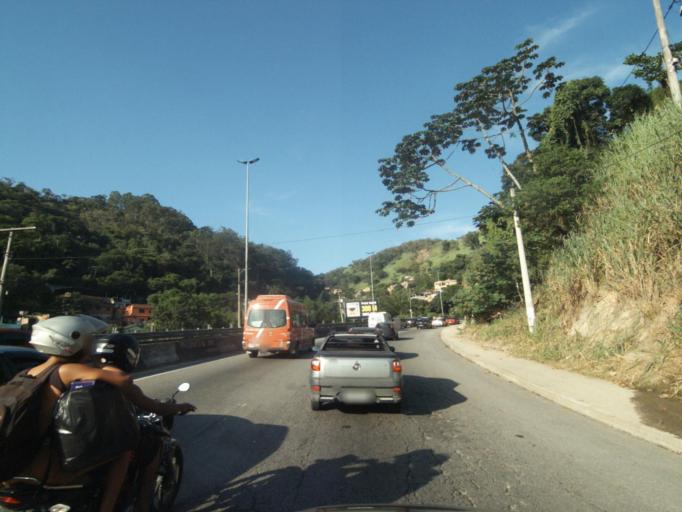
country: BR
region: Rio de Janeiro
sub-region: Niteroi
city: Niteroi
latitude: -22.8812
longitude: -43.0735
